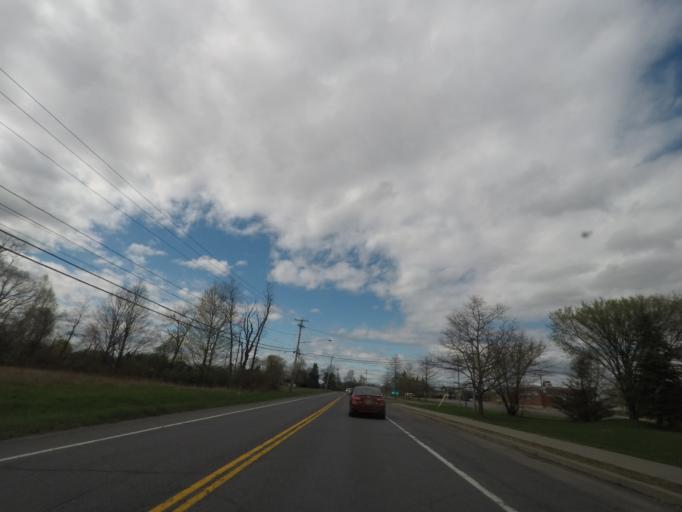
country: US
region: New York
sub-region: Columbia County
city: Valatie
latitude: 42.4231
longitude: -73.6857
